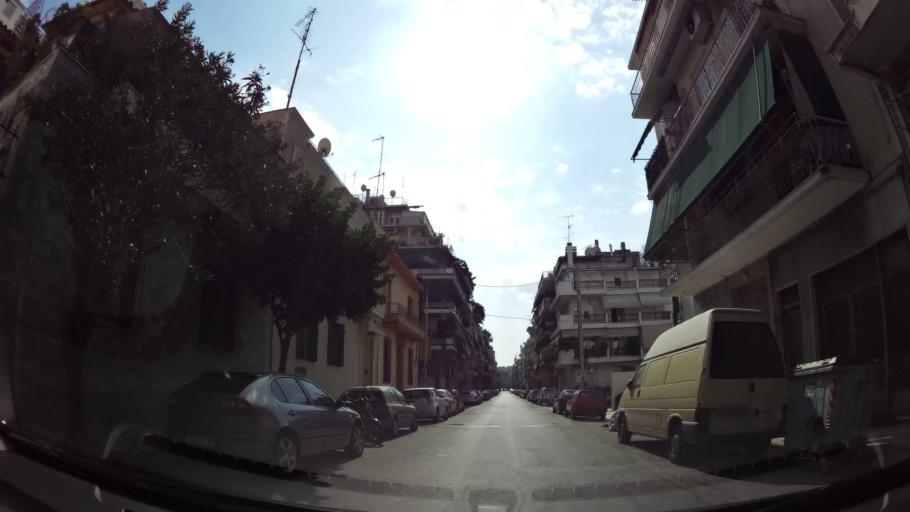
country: GR
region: Attica
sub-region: Nomarchia Athinas
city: Athens
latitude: 37.9974
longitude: 23.7181
